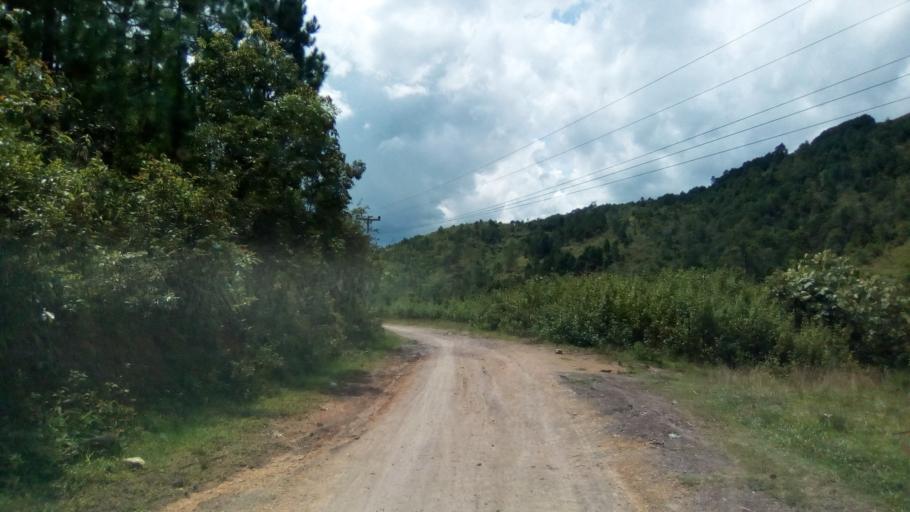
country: LA
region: Xiangkhoang
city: Muang Phonsavan
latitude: 19.3398
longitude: 103.6249
